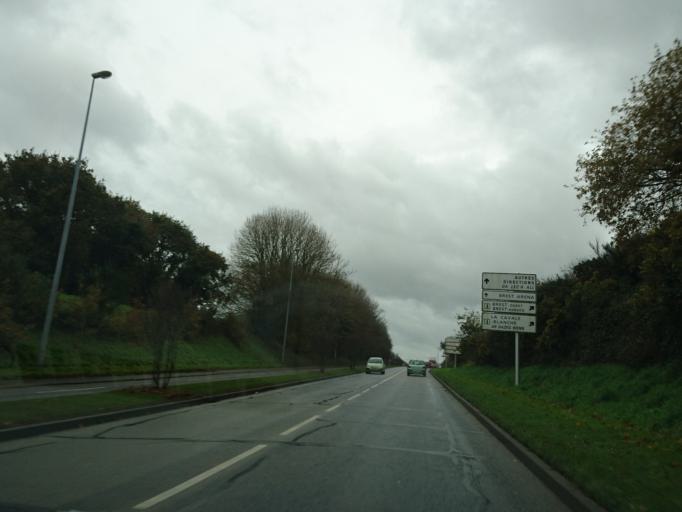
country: FR
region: Brittany
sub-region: Departement du Finistere
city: Bohars
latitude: 48.3996
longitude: -4.5268
